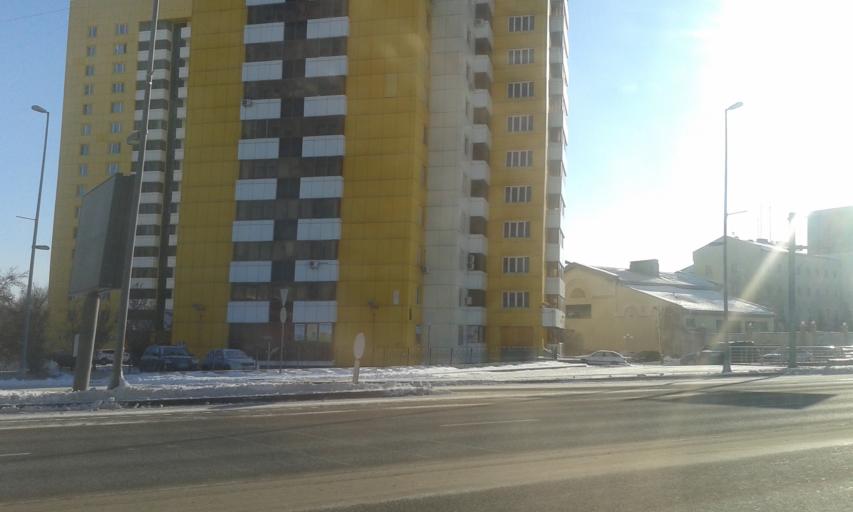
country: KZ
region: Astana Qalasy
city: Astana
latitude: 51.1554
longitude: 71.4337
